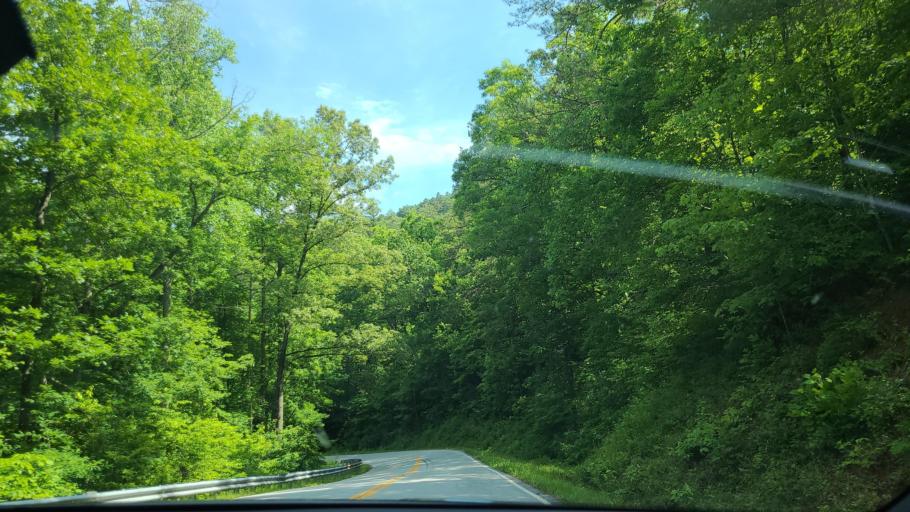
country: US
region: South Carolina
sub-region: Oconee County
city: Walhalla
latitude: 34.8979
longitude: -83.1773
